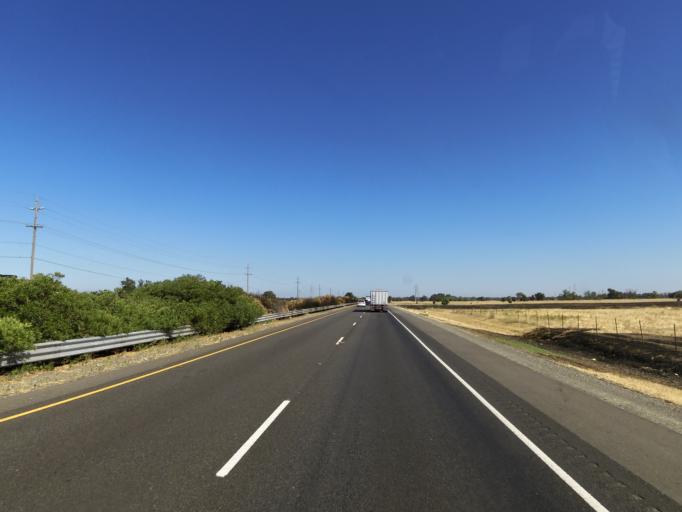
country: US
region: California
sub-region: Sacramento County
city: Galt
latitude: 38.3272
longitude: -121.3280
